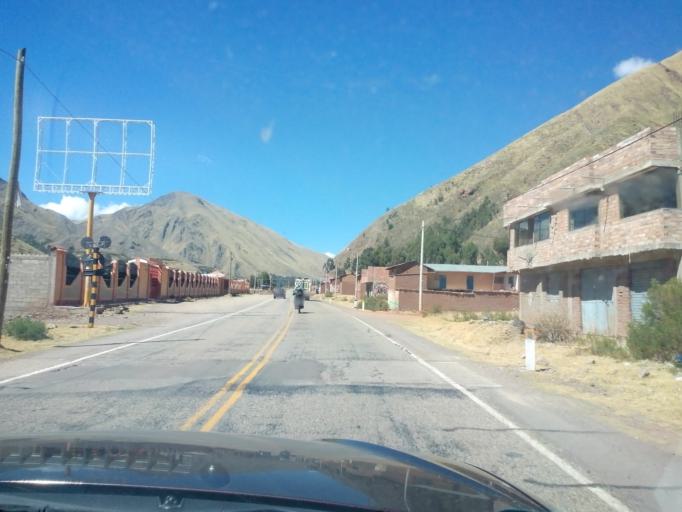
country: PE
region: Cusco
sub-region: Provincia de Canchis
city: Marangani
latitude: -14.3585
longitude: -71.1647
